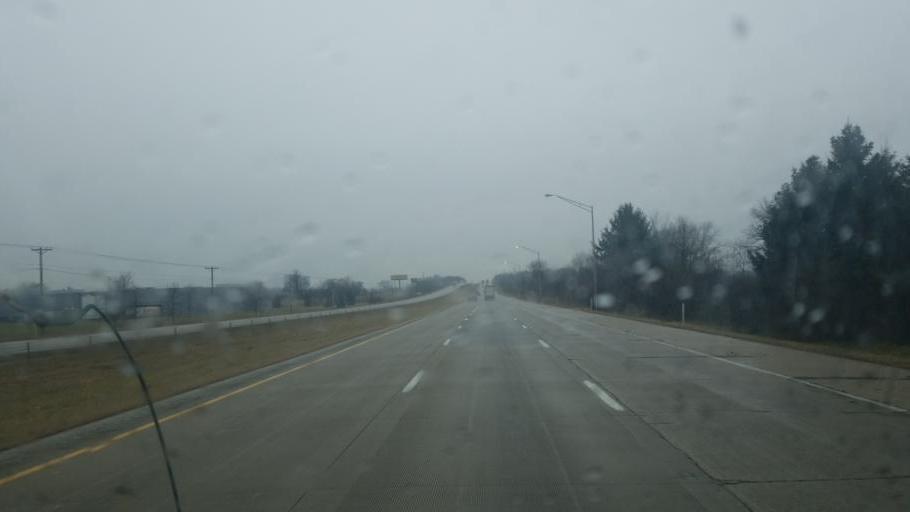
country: US
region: Indiana
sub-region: Wayne County
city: Centerville
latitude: 39.8637
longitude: -84.9515
